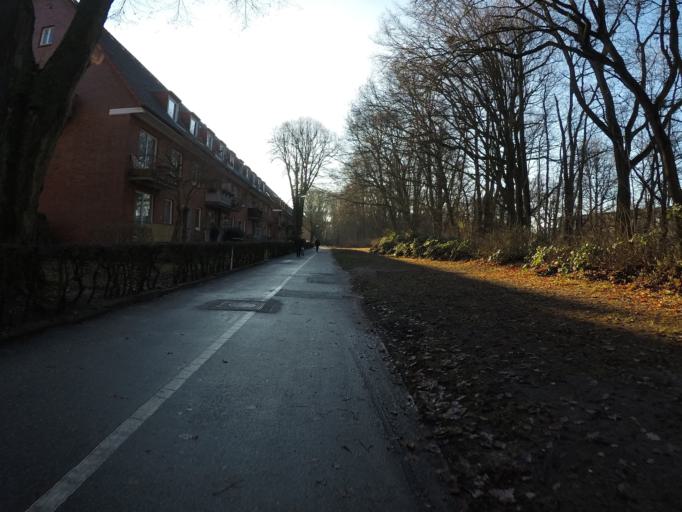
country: DE
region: Hamburg
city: Fuhlsbuettel
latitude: 53.6483
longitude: 10.0177
